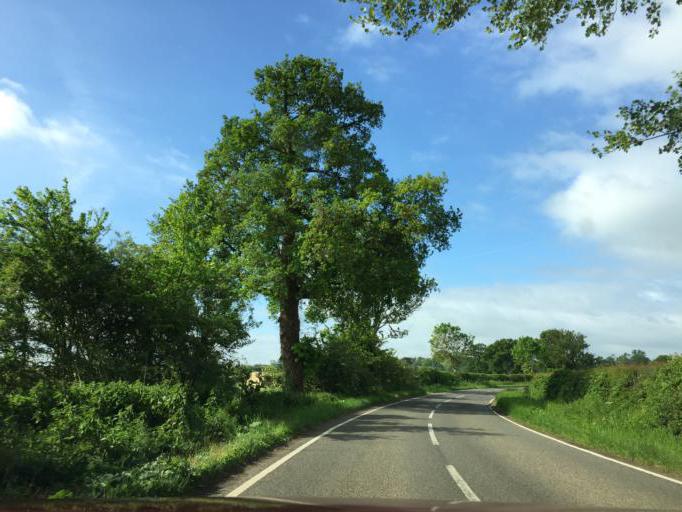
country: GB
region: England
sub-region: Northamptonshire
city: Towcester
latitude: 52.1308
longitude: -0.9578
